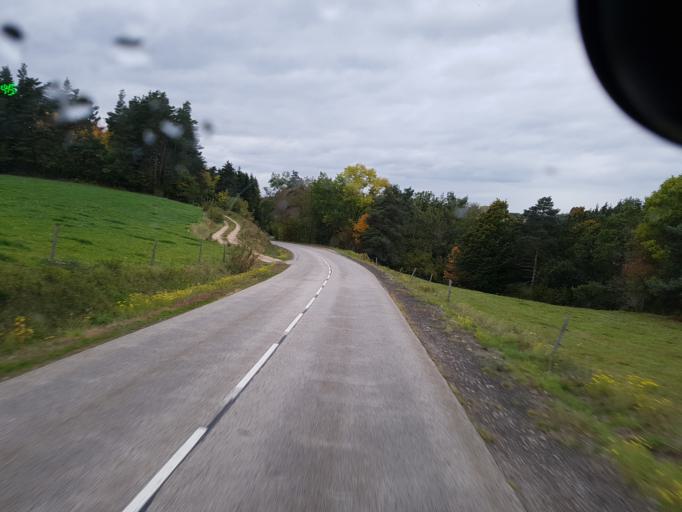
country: FR
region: Auvergne
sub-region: Departement de la Haute-Loire
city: Sainte-Sigolene
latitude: 45.2304
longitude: 4.2069
